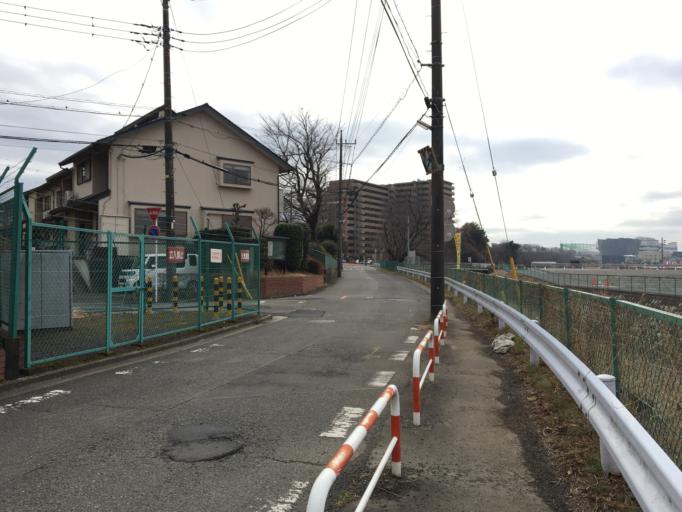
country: JP
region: Saitama
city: Tokorozawa
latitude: 35.8049
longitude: 139.5135
